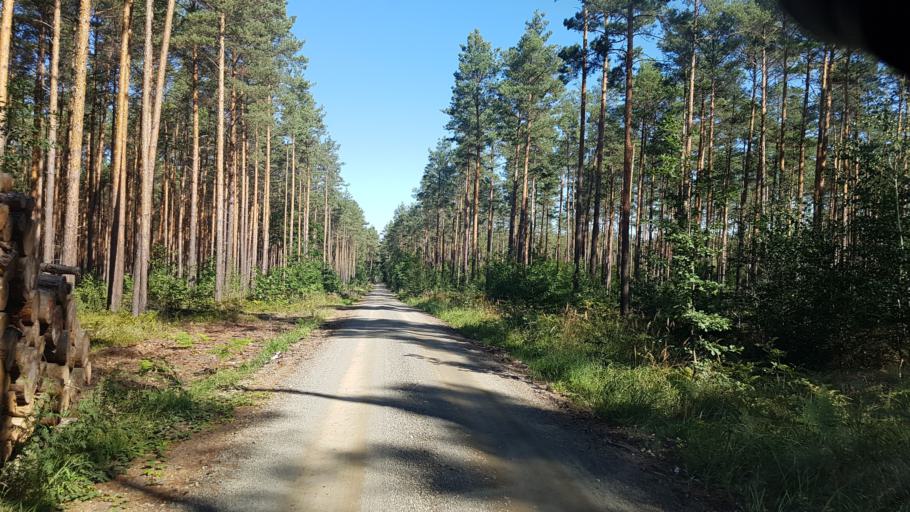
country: DE
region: Brandenburg
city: Hohenleipisch
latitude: 51.5359
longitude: 13.5819
